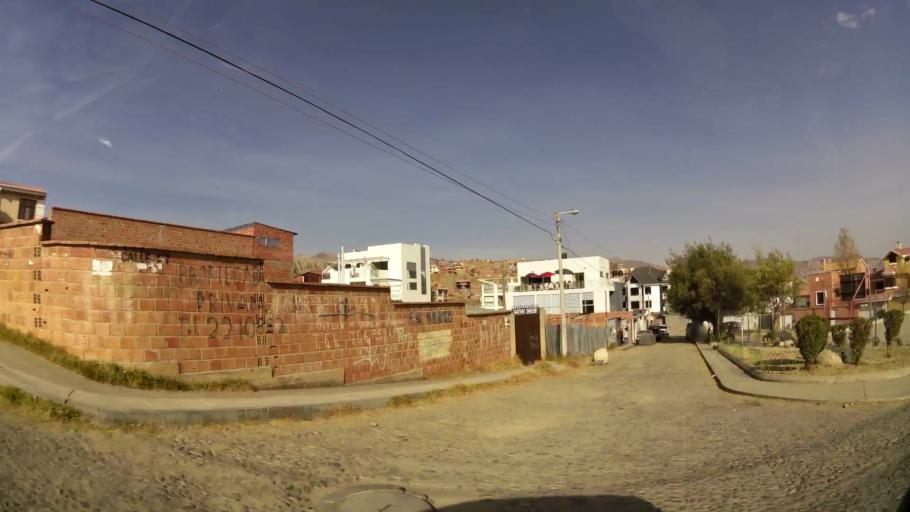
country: BO
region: La Paz
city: La Paz
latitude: -16.5088
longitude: -68.0838
